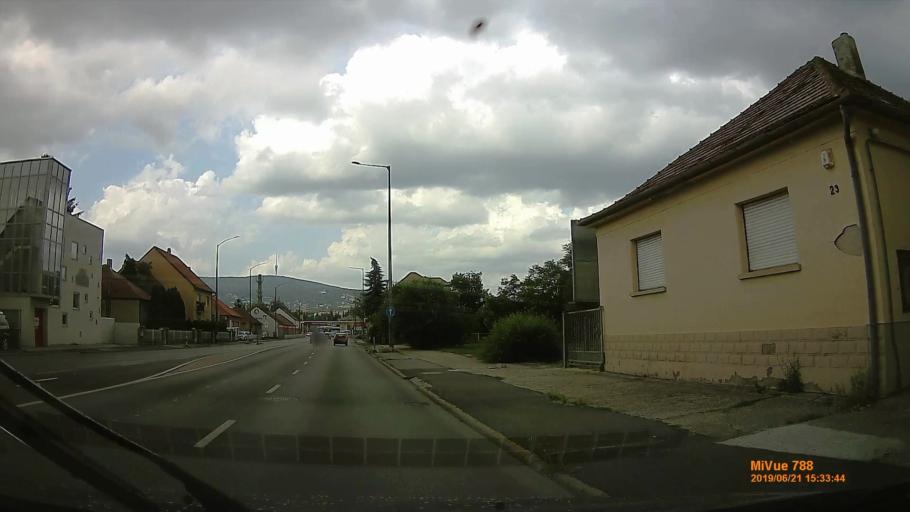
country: HU
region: Baranya
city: Pecs
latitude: 46.0579
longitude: 18.2308
